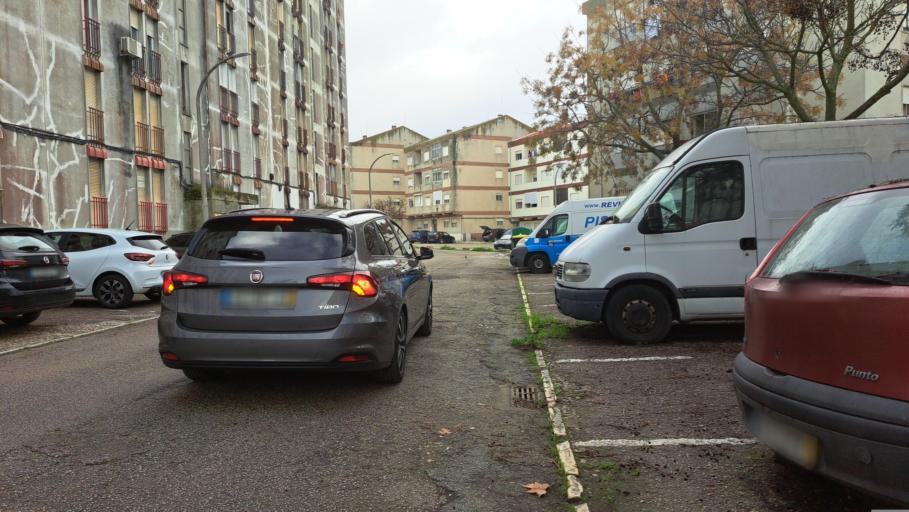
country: PT
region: Setubal
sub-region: Moita
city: Alhos Vedros
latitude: 38.6466
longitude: -9.0418
